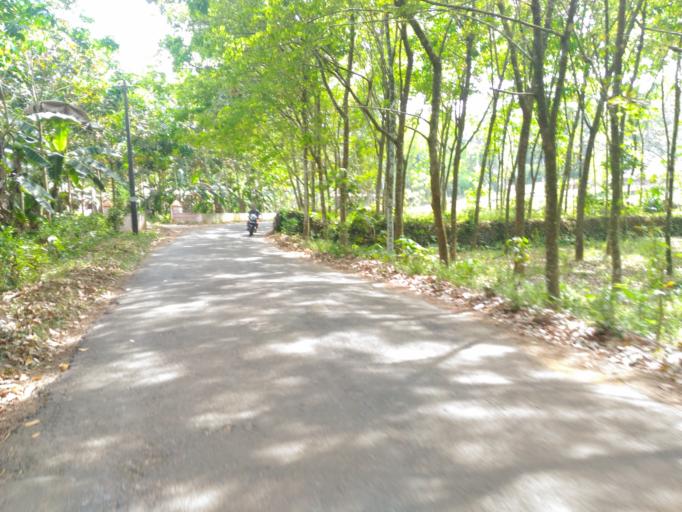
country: IN
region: Kerala
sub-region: Kottayam
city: Palackattumala
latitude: 9.8726
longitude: 76.6494
